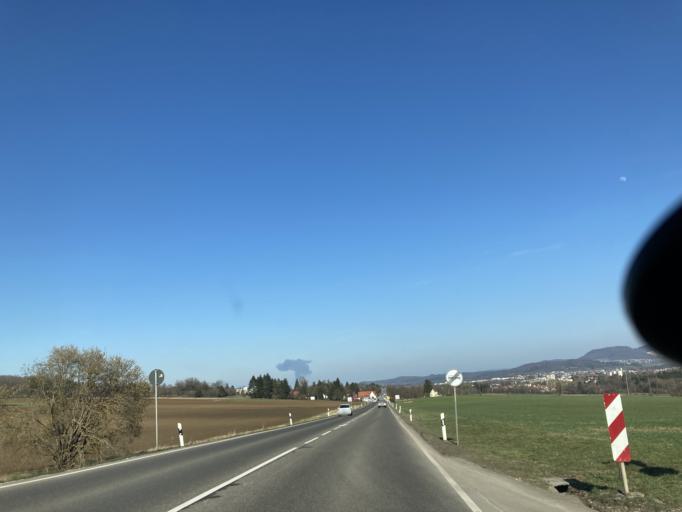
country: DE
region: Baden-Wuerttemberg
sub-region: Tuebingen Region
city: Bodelshausen
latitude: 48.3955
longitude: 9.0041
